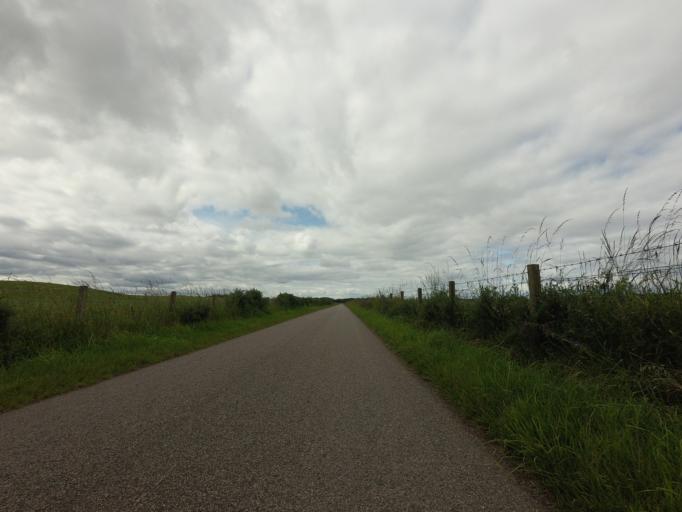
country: GB
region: Scotland
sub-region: Moray
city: Kinloss
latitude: 57.6308
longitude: -3.5391
